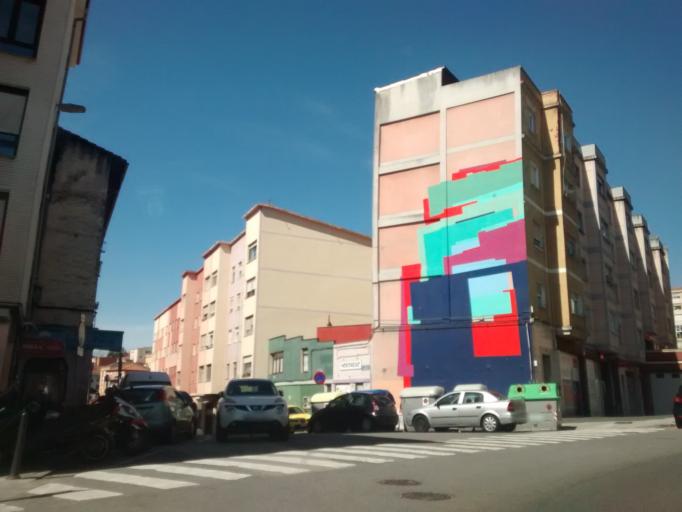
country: ES
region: Cantabria
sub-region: Provincia de Cantabria
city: Santander
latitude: 43.4639
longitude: -3.8147
